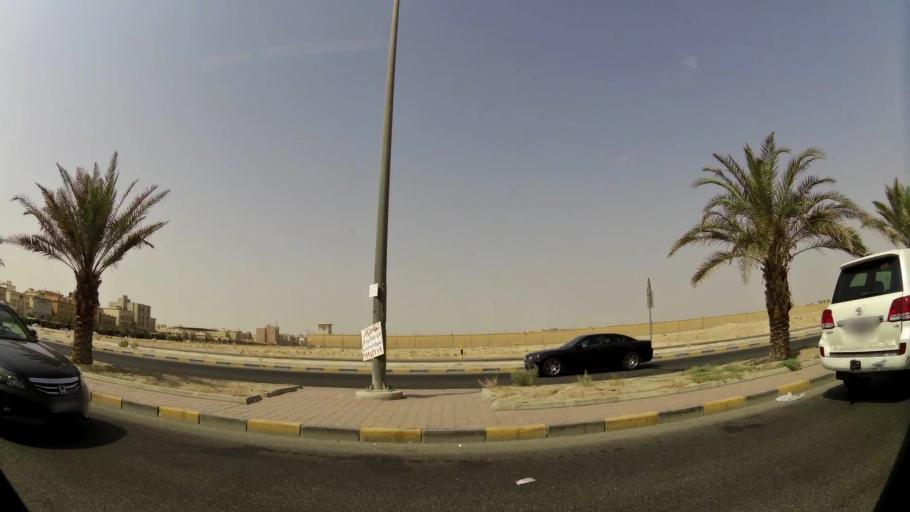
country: KW
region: Muhafazat al Jahra'
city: Al Jahra'
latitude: 29.3098
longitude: 47.7057
